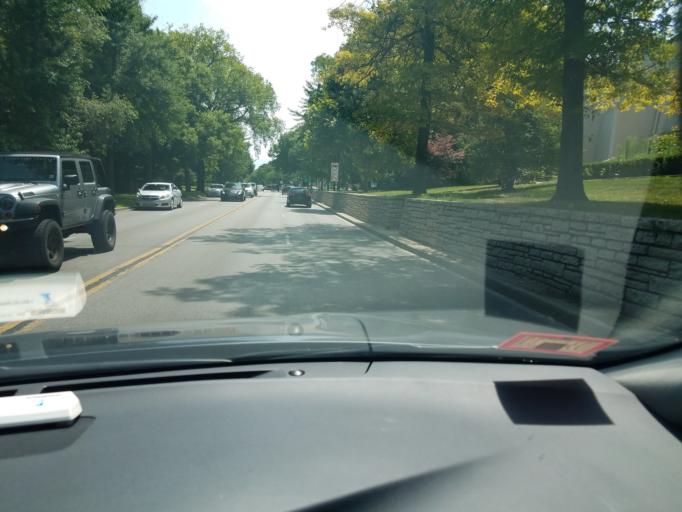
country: US
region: Illinois
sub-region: Cook County
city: Evanston
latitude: 42.0427
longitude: -87.6885
